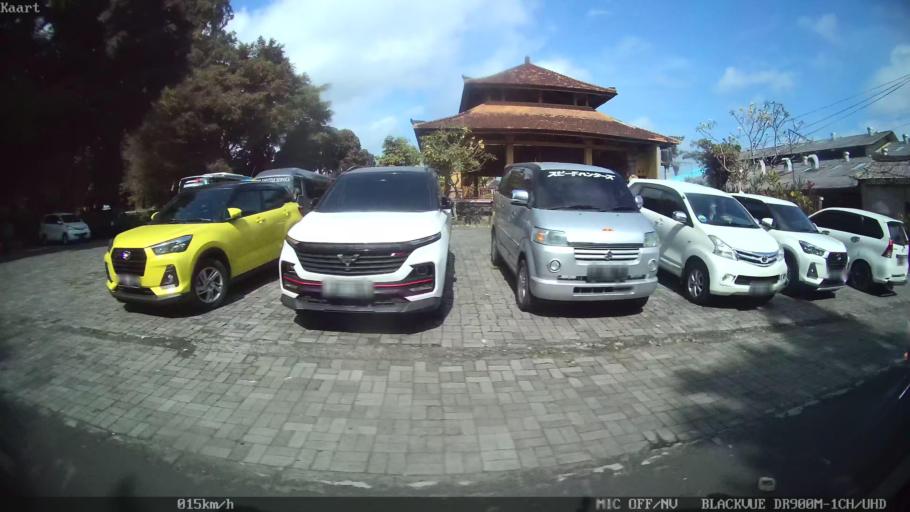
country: ID
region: Bali
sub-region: Kabupaten Gianyar
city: Ubud
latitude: -8.5095
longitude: 115.2692
